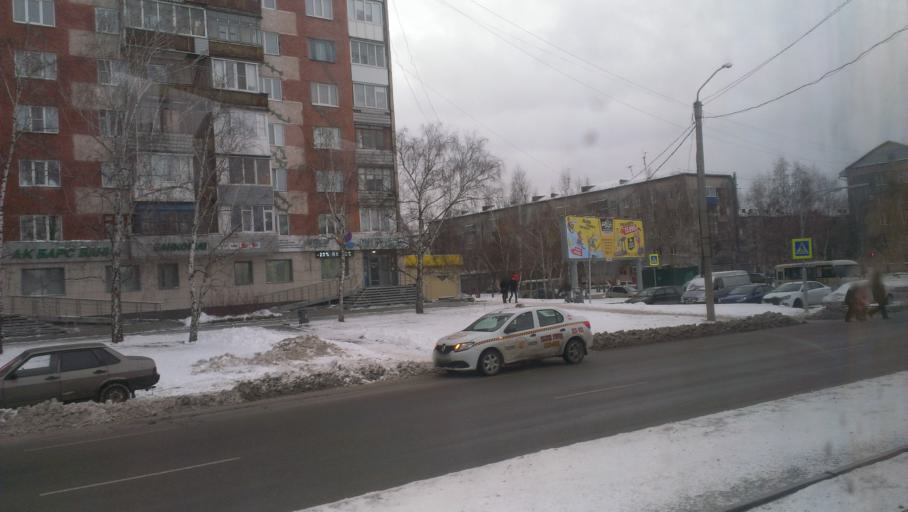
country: RU
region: Altai Krai
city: Novosilikatnyy
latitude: 53.3673
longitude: 83.6768
